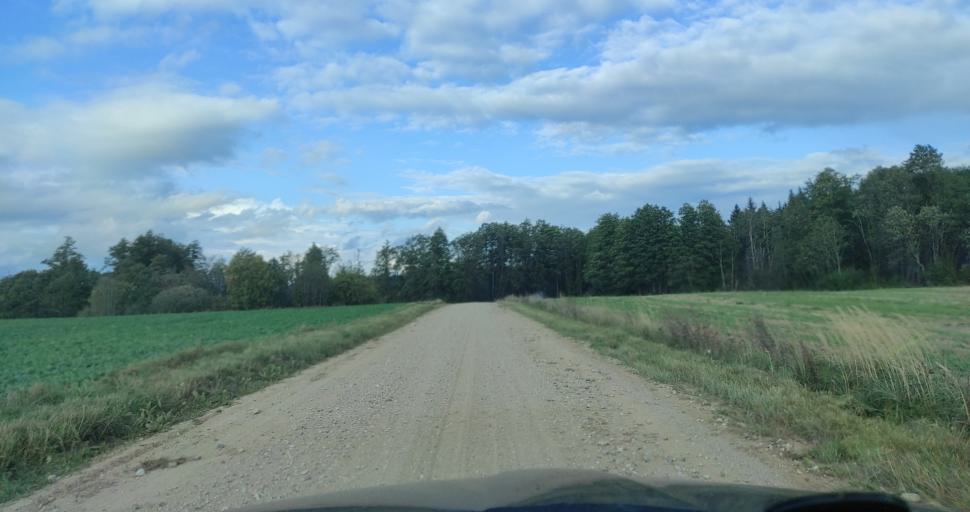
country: LV
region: Talsu Rajons
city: Sabile
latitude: 56.9016
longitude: 22.4319
